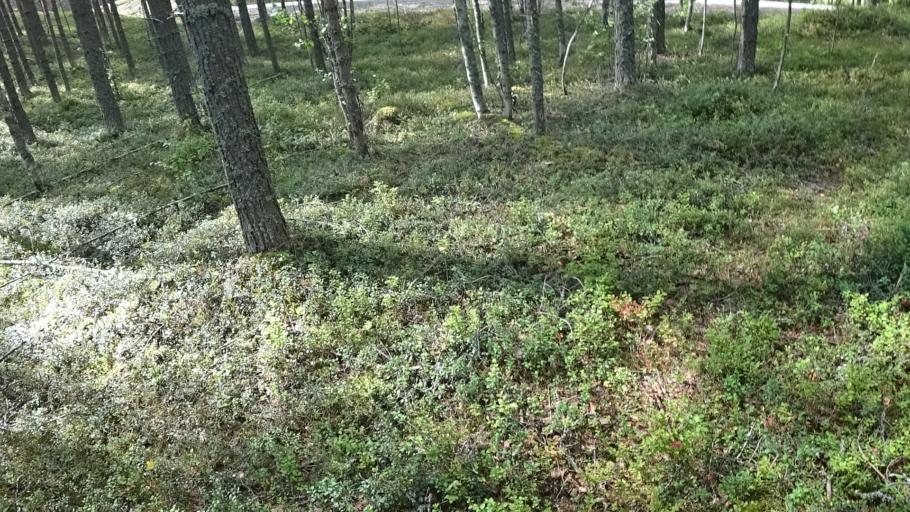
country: FI
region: North Karelia
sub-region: Joensuu
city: Ilomantsi
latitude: 62.6085
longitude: 31.1859
